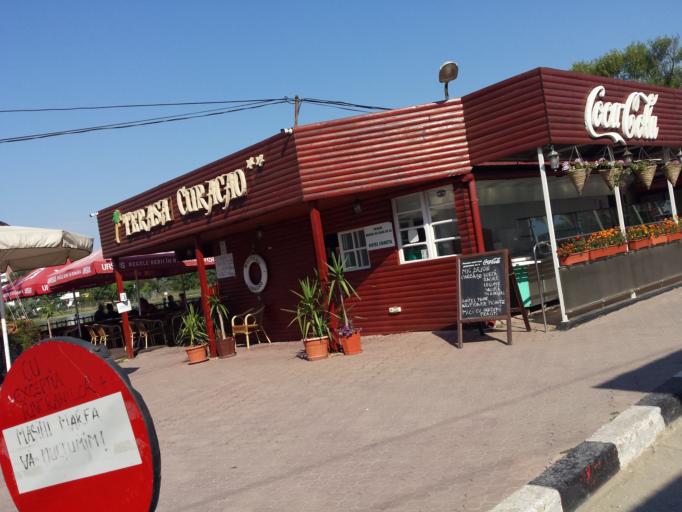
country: RO
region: Constanta
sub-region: Comuna Douazeci si Trei August
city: Douazeci si Trei August
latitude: 43.8588
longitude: 28.6061
